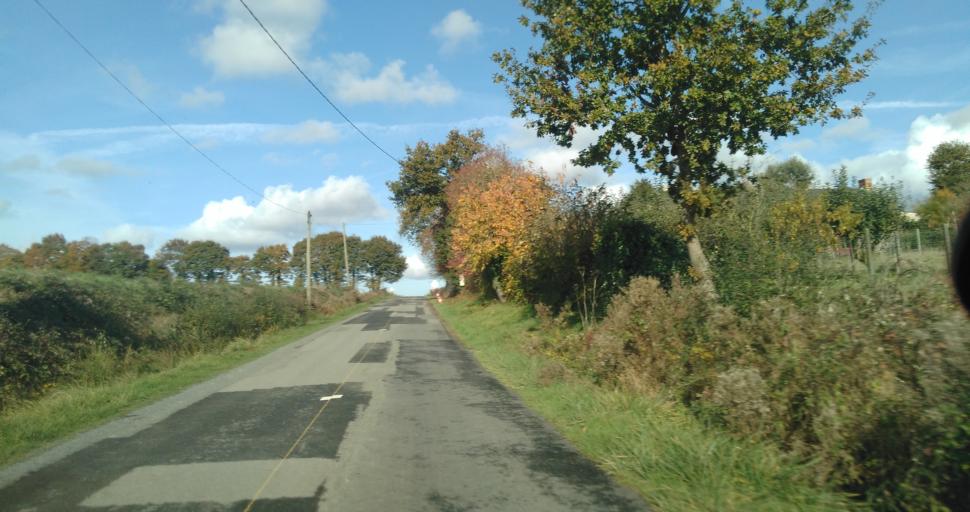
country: FR
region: Brittany
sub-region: Departement d'Ille-et-Vilaine
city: Iffendic
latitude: 48.1176
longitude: -2.0871
